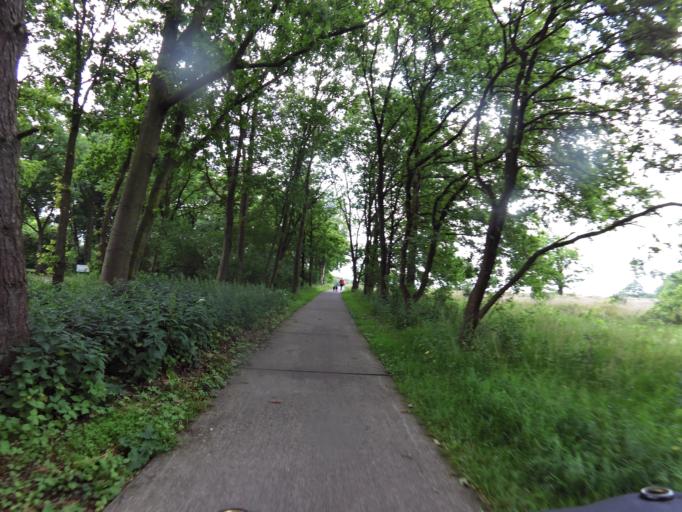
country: NL
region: Gelderland
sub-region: Gemeente Nunspeet
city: Nunspeet
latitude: 52.3256
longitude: 5.8193
